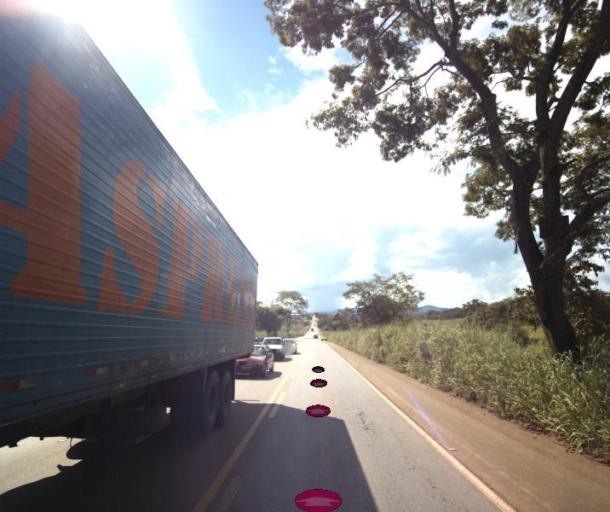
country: BR
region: Goias
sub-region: Jaragua
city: Jaragua
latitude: -15.7685
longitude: -49.3092
